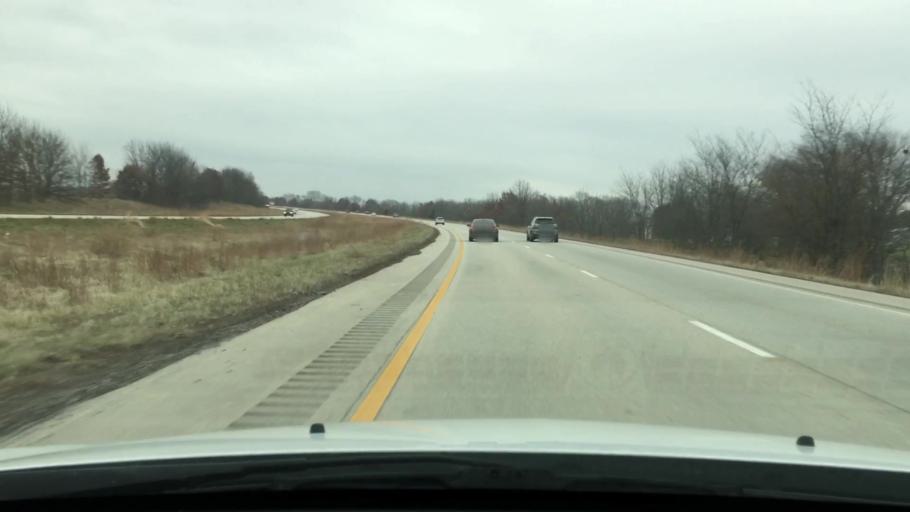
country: US
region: Illinois
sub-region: Sangamon County
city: New Berlin
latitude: 39.7416
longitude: -89.8256
